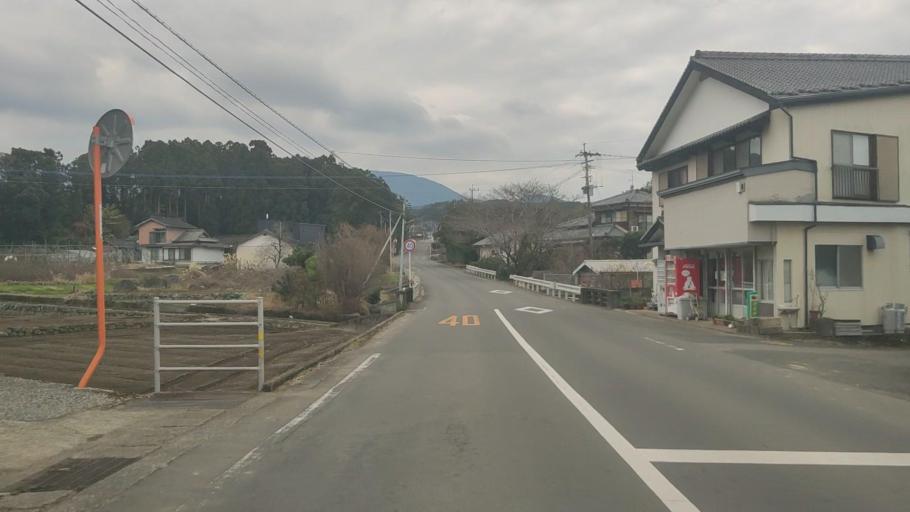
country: JP
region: Nagasaki
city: Shimabara
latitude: 32.8374
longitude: 130.2945
